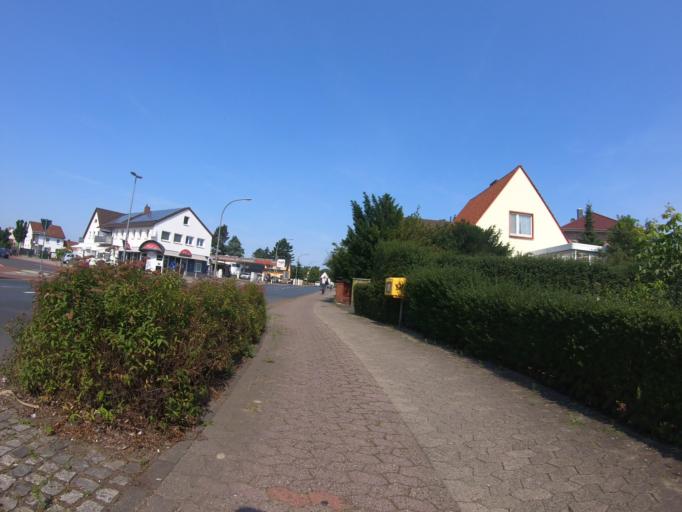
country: DE
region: Lower Saxony
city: Gifhorn
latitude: 52.4750
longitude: 10.5576
